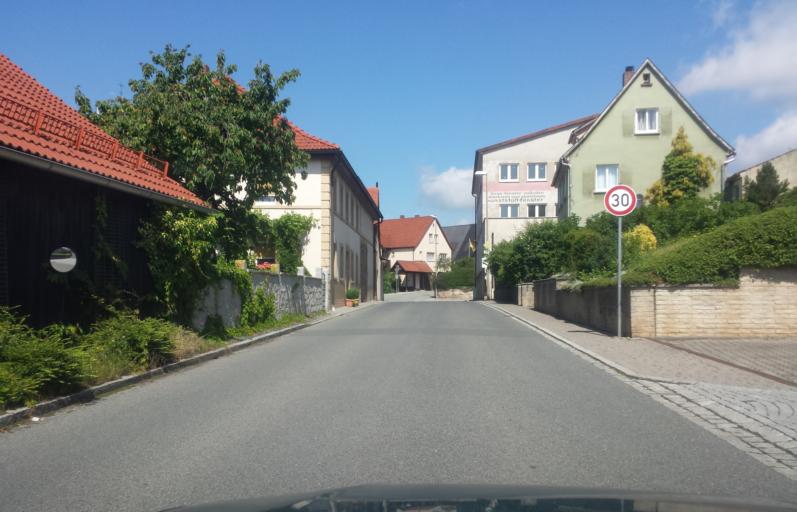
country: DE
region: Bavaria
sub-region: Upper Franconia
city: Burgkunstadt
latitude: 50.1410
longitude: 11.2545
